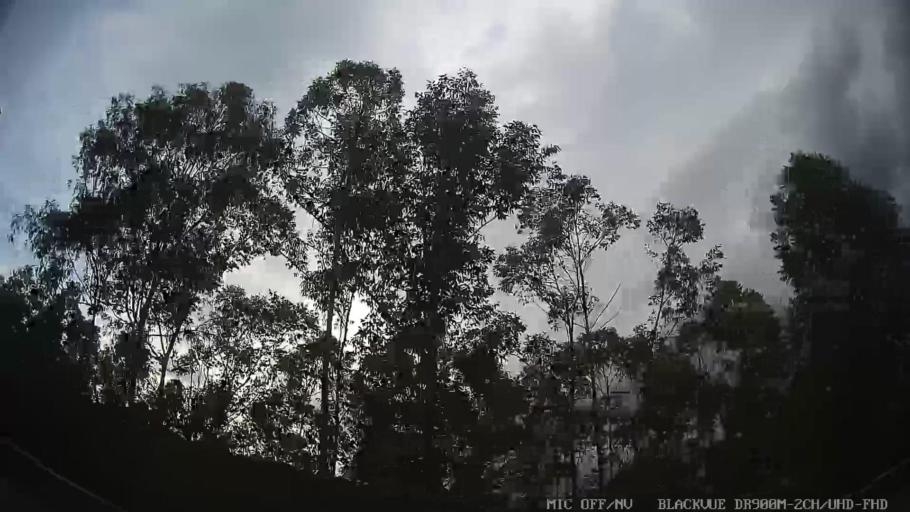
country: BR
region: Sao Paulo
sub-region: Itatiba
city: Itatiba
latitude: -22.9365
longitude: -46.7967
